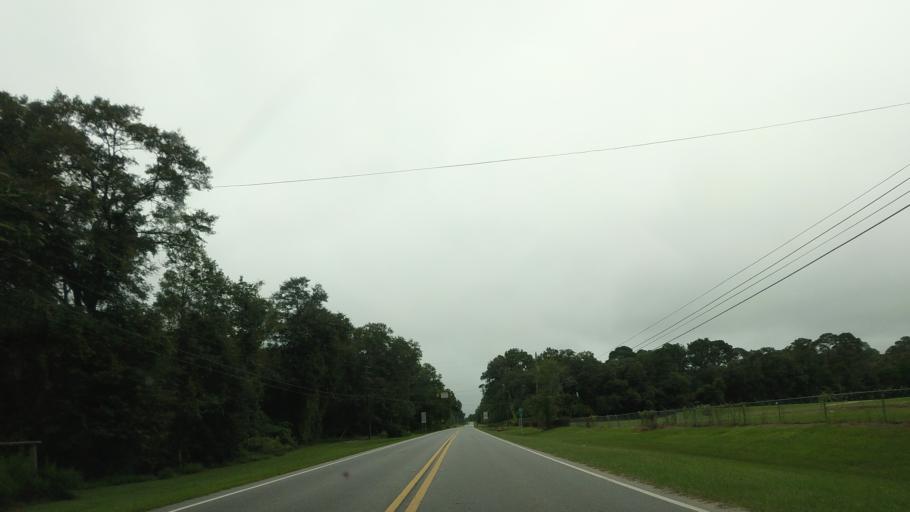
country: US
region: Georgia
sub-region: Berrien County
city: Nashville
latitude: 31.2201
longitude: -83.2486
